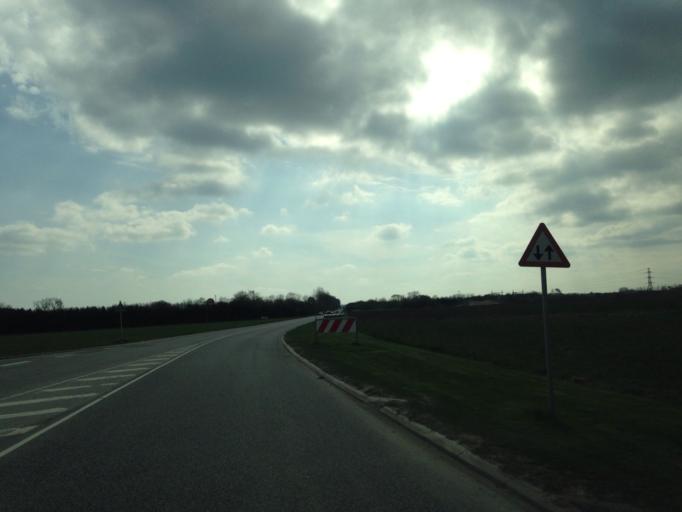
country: DK
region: Zealand
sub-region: Greve Kommune
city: Greve
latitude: 55.6152
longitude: 12.3128
